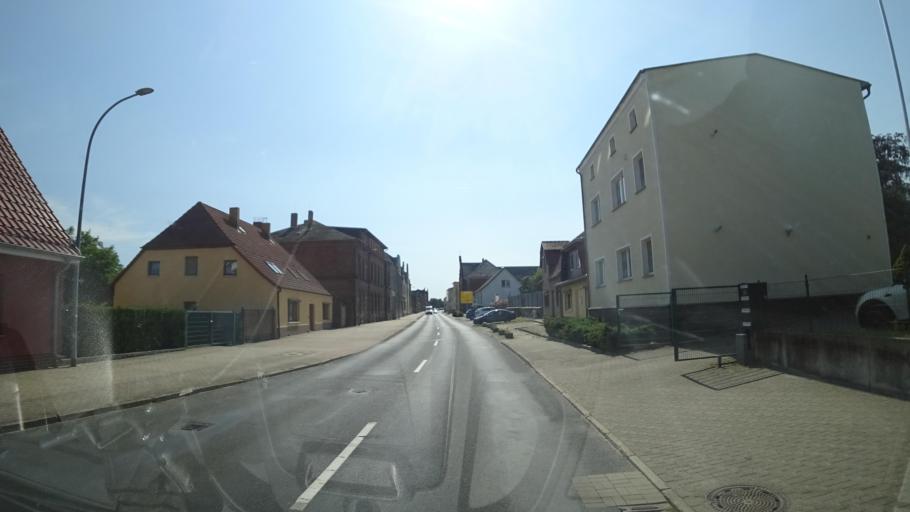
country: DE
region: Mecklenburg-Vorpommern
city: Wolgast
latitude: 54.0543
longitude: 13.7704
